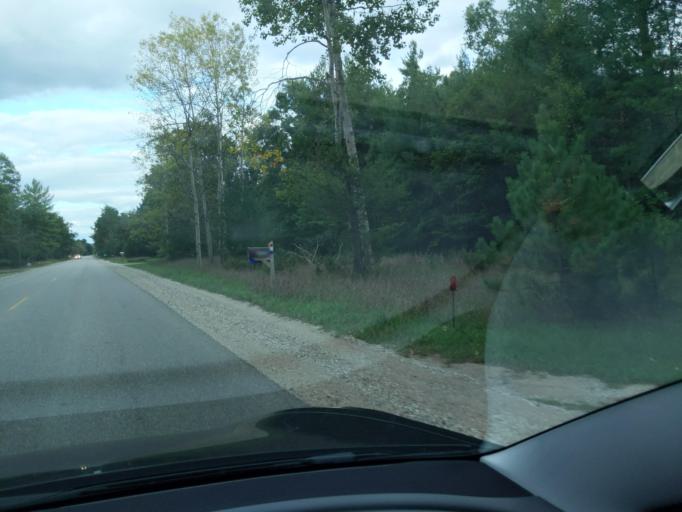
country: US
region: Michigan
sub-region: Kalkaska County
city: Rapid City
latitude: 44.8411
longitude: -85.3001
